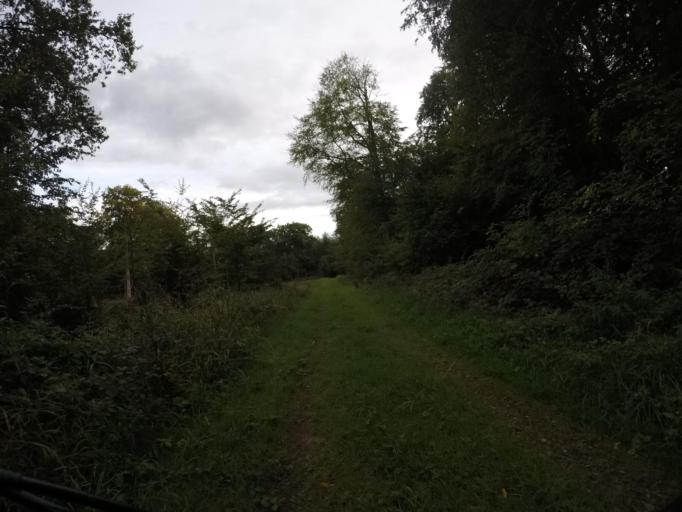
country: DE
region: Lower Saxony
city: Neu Darchau
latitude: 53.2768
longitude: 10.8913
